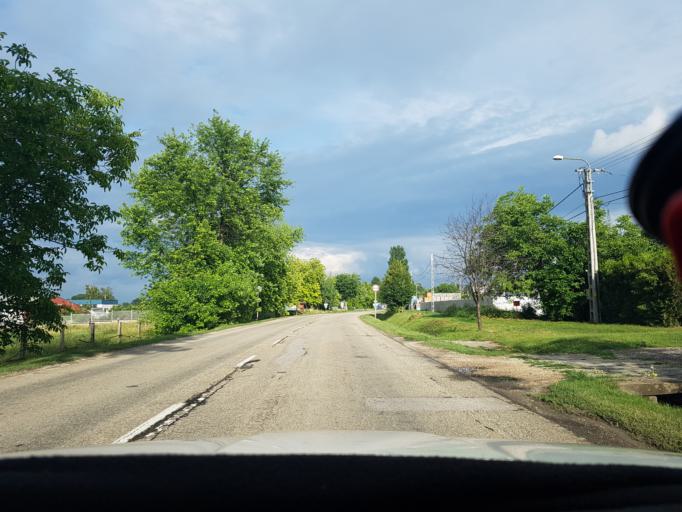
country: HU
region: Komarom-Esztergom
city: Sutto
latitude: 47.7562
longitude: 18.4589
